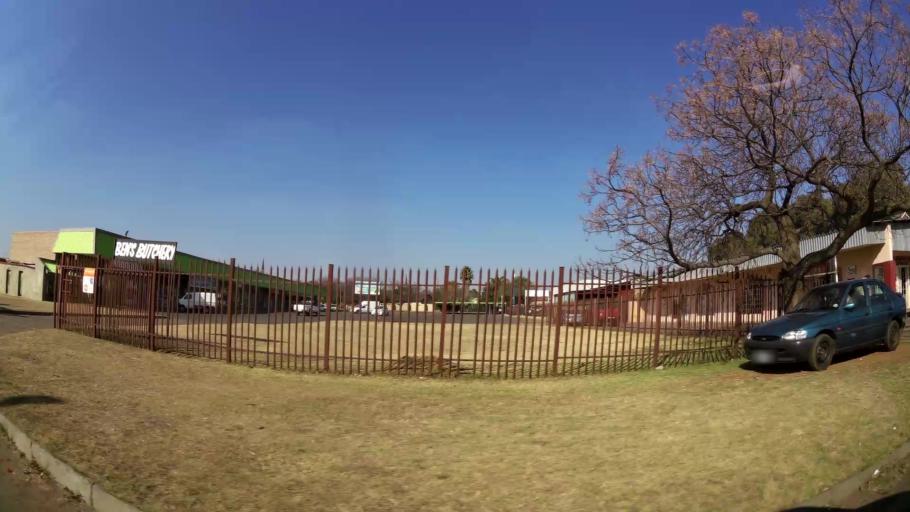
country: ZA
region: Gauteng
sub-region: West Rand District Municipality
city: Randfontein
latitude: -26.1761
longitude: 27.6924
